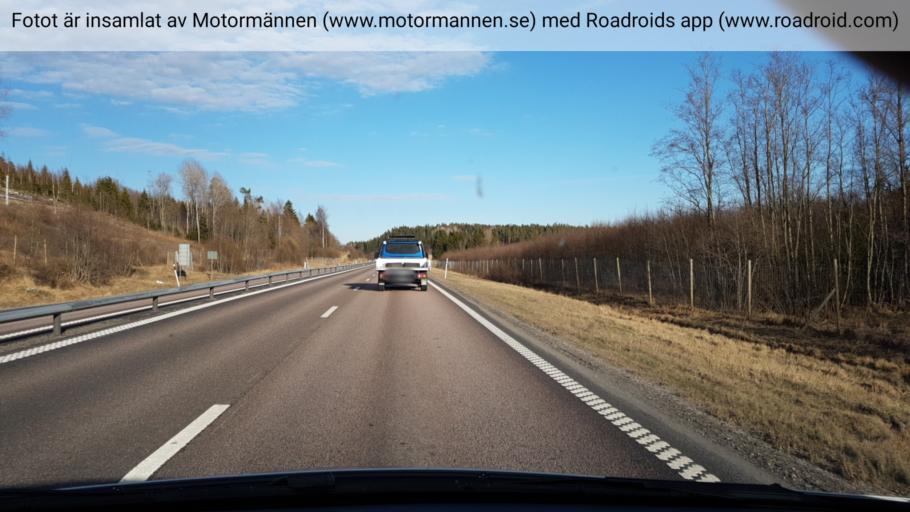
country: SE
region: Vaesternorrland
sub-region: OErnskoeldsviks Kommun
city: Ornskoldsvik
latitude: 63.3140
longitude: 18.8157
